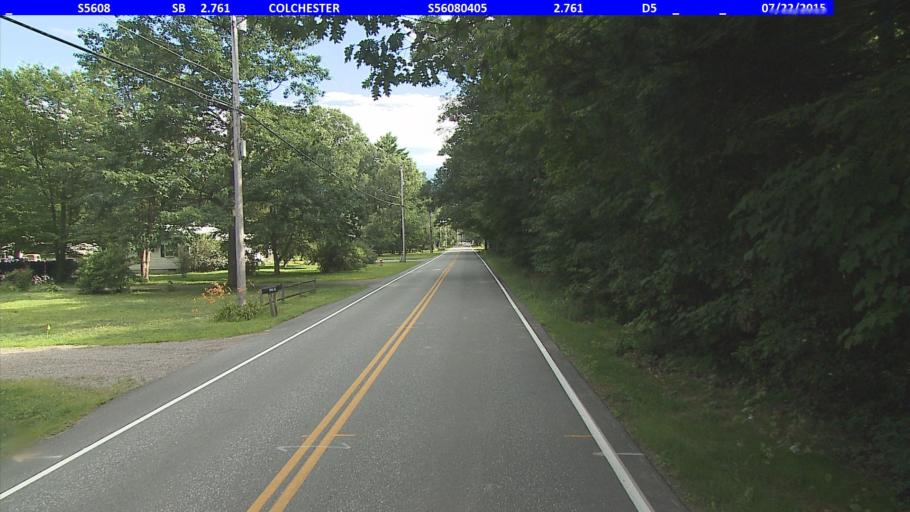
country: US
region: Vermont
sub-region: Chittenden County
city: Winooski
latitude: 44.5365
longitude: -73.2090
